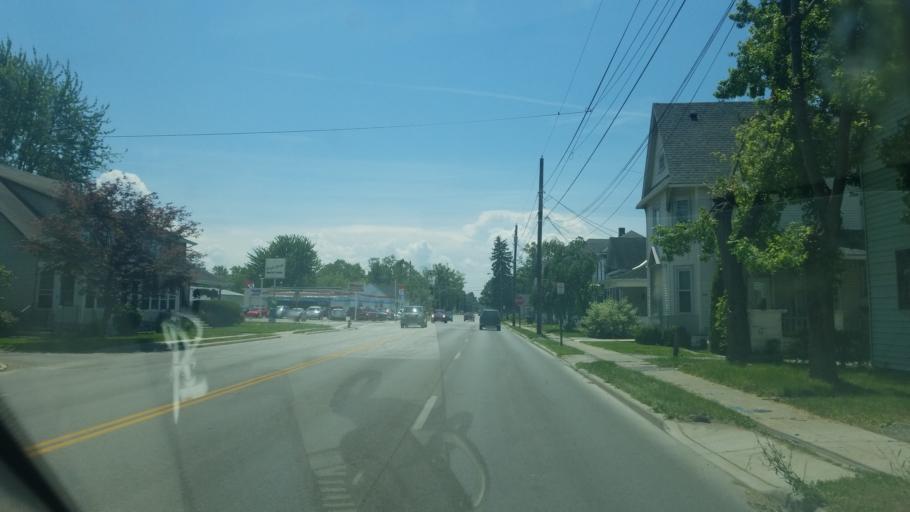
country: US
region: Ohio
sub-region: Hancock County
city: Findlay
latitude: 41.0320
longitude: -83.6412
